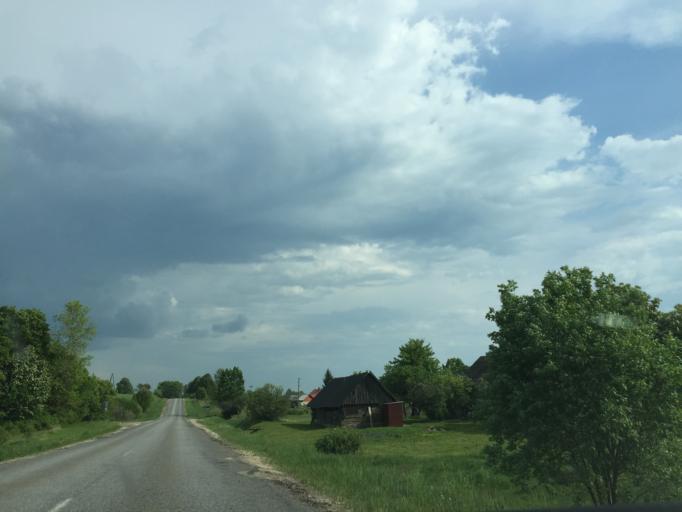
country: LV
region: Rezekne
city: Rezekne
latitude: 56.3589
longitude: 27.4849
